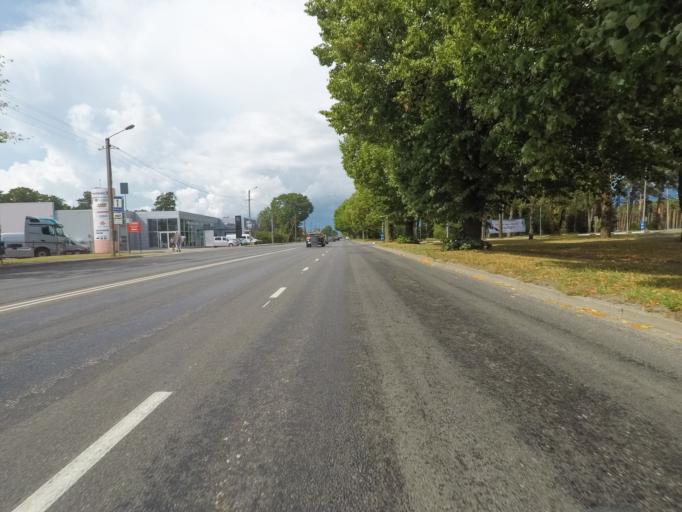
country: EE
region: Paernumaa
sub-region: Paernu linn
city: Parnu
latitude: 58.3632
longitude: 24.5607
